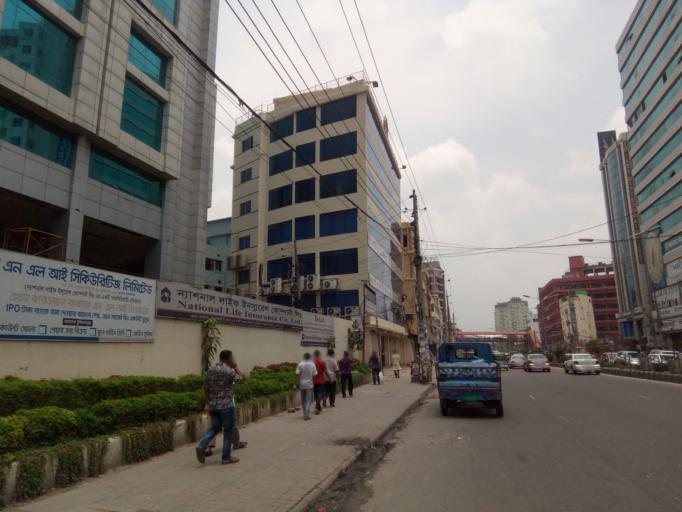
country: BD
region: Dhaka
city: Azimpur
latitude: 23.7539
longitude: 90.3915
